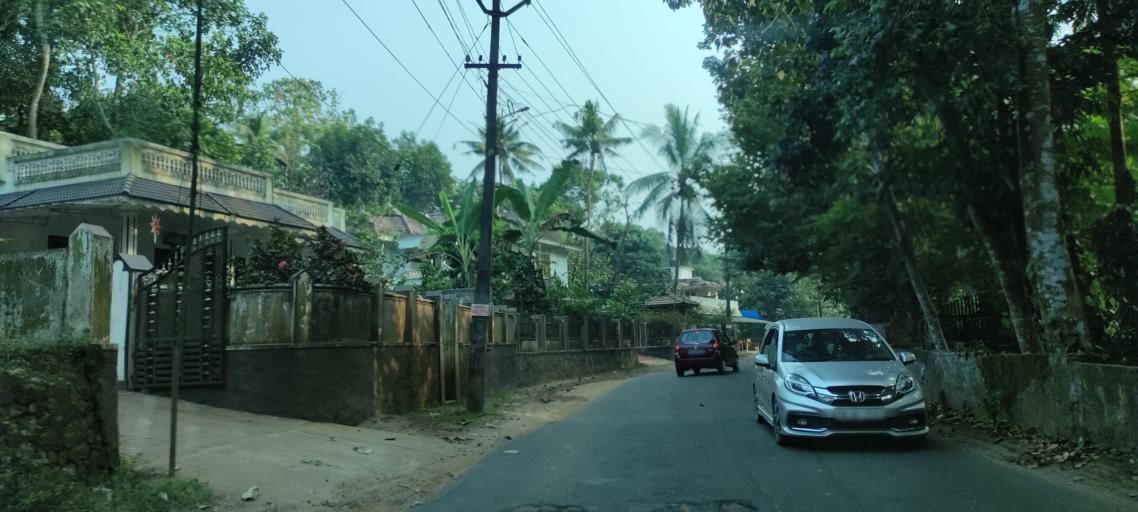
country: IN
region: Kerala
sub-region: Kottayam
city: Vaikam
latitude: 9.7078
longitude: 76.4781
